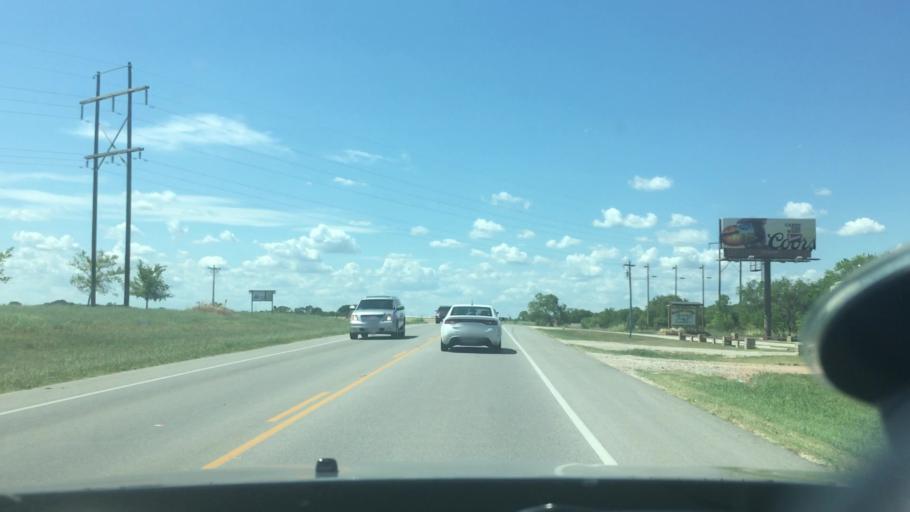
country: US
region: Oklahoma
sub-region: Marshall County
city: Kingston
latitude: 34.0409
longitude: -96.7355
